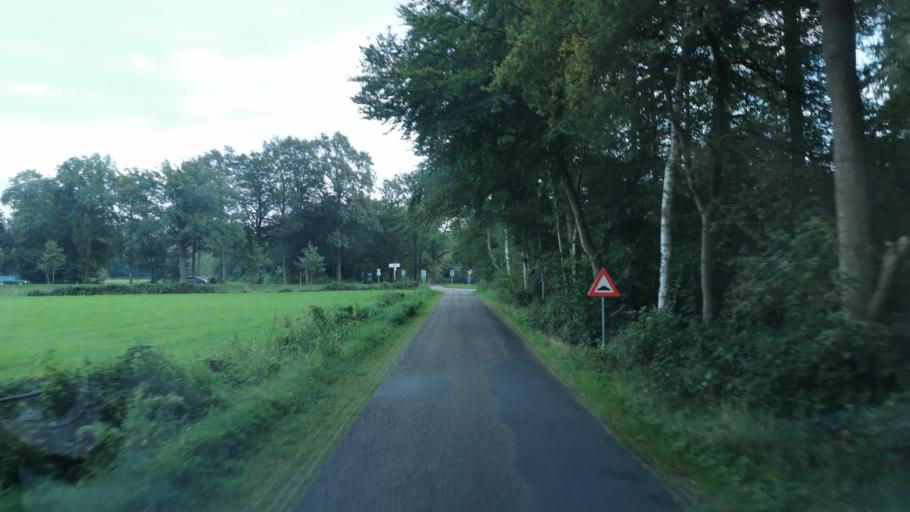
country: NL
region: Overijssel
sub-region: Gemeente Oldenzaal
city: Oldenzaal
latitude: 52.3303
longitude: 6.9483
